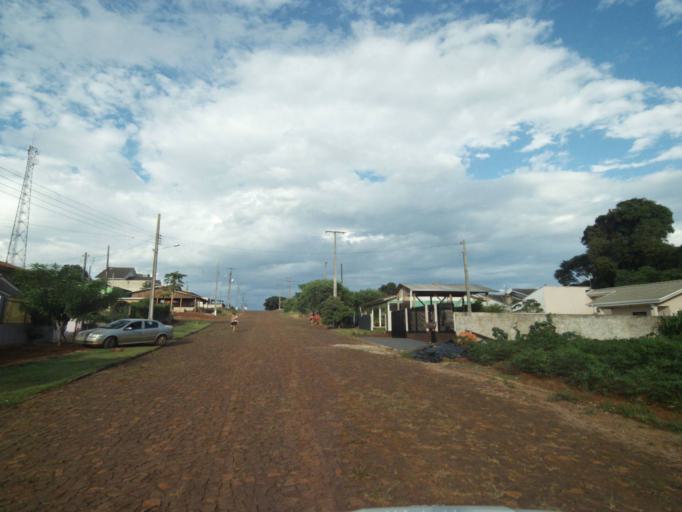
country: BR
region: Parana
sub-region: Laranjeiras Do Sul
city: Laranjeiras do Sul
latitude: -25.4963
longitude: -52.5338
